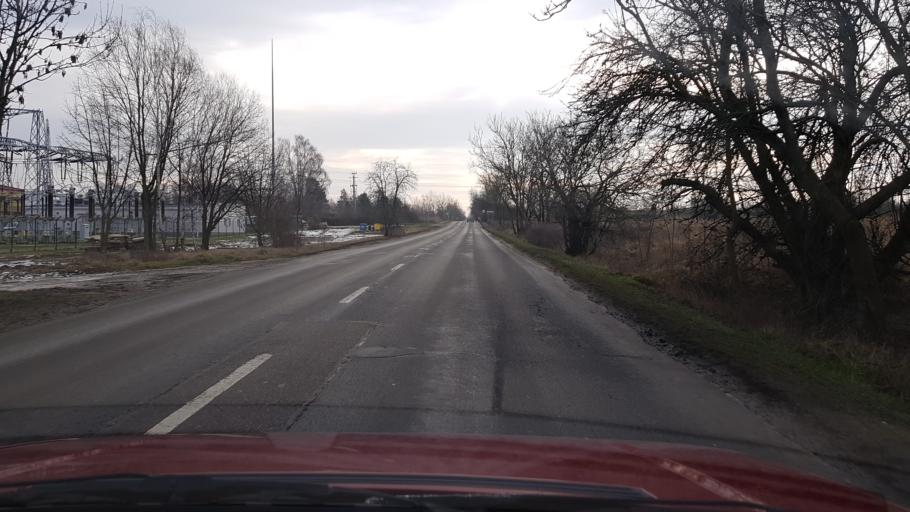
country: PL
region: West Pomeranian Voivodeship
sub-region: Powiat policki
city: Police
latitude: 53.5006
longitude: 14.5786
